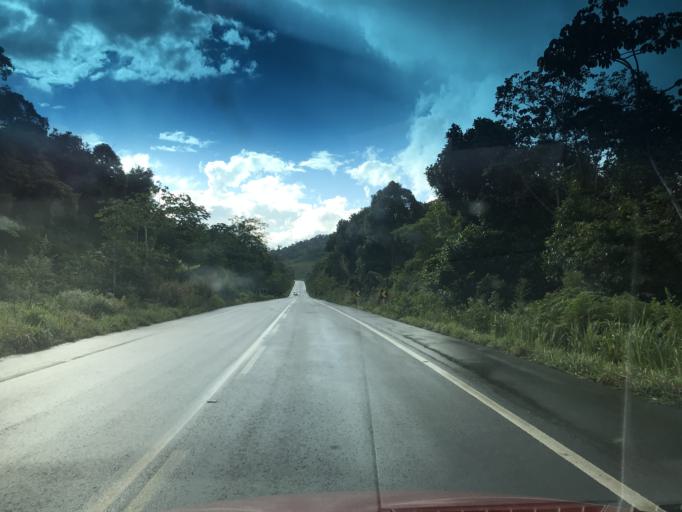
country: BR
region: Bahia
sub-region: Ibirapitanga
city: Ibirapitanga
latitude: -14.0000
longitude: -39.4479
